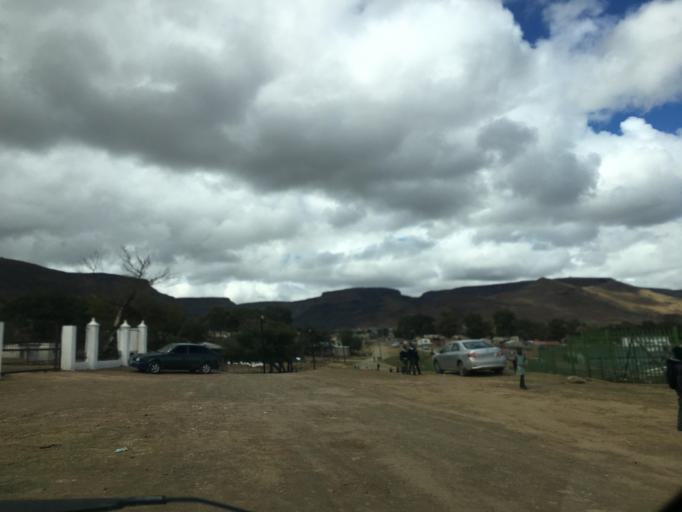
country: ZA
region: Eastern Cape
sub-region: Chris Hani District Municipality
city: Cala
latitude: -31.5240
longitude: 27.6884
